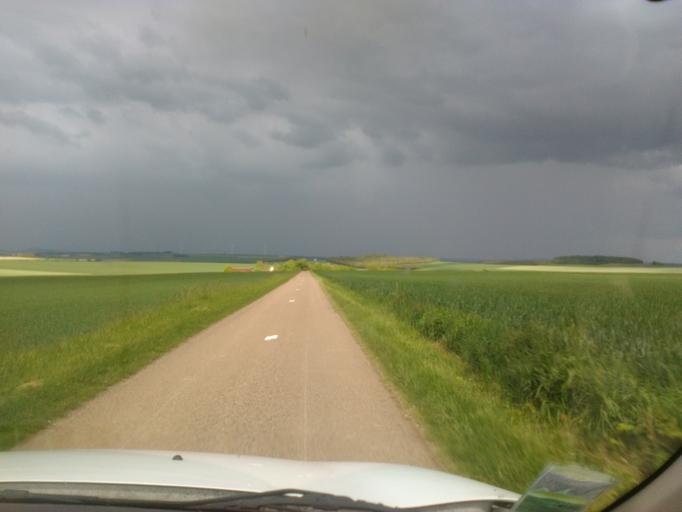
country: FR
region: Champagne-Ardenne
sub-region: Departement de l'Aube
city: Nogent-sur-Seine
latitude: 48.3788
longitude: 3.4917
